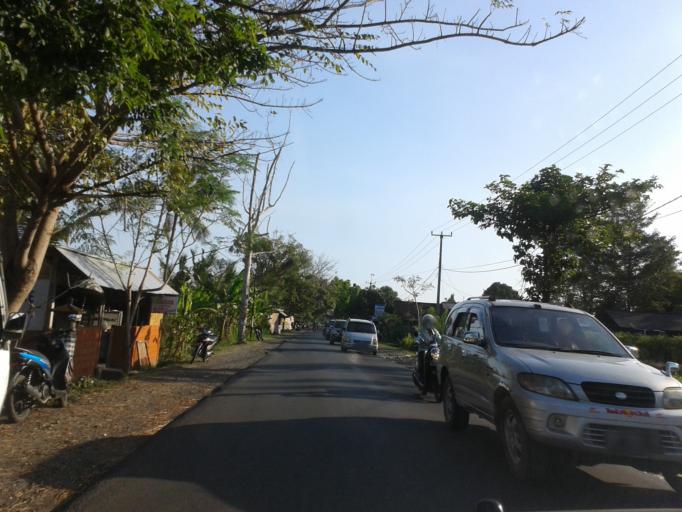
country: ID
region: Bali
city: Banjar Wangsian
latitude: -8.5050
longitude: 115.4034
